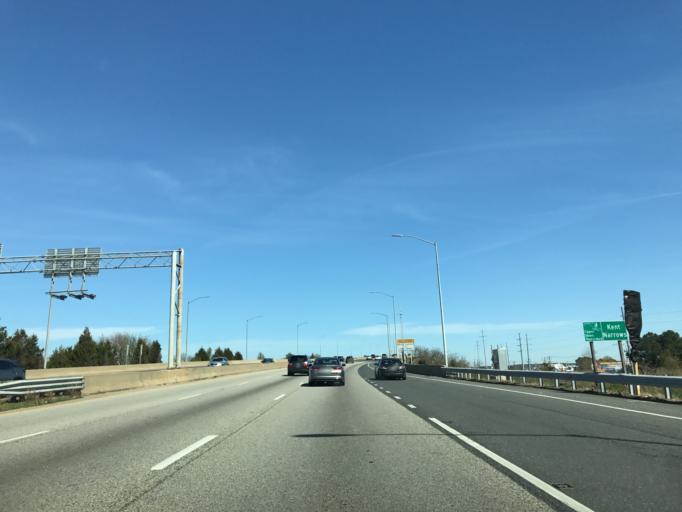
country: US
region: Maryland
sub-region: Queen Anne's County
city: Chester
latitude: 38.9721
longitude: -76.2551
